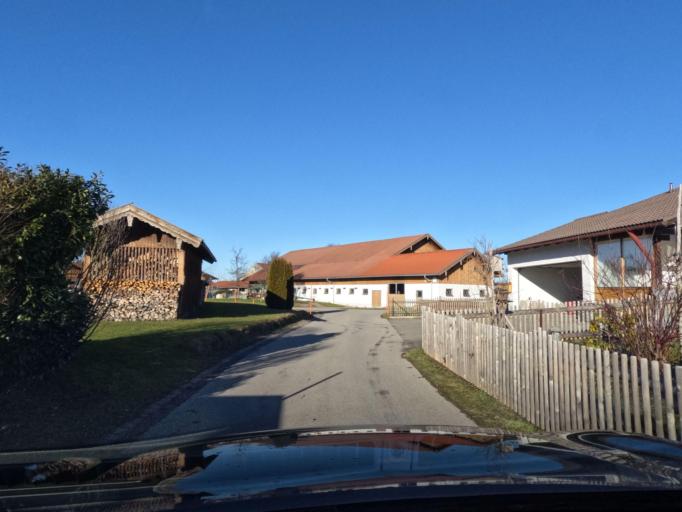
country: DE
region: Bavaria
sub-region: Upper Bavaria
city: Surberg
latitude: 47.8802
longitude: 12.6889
